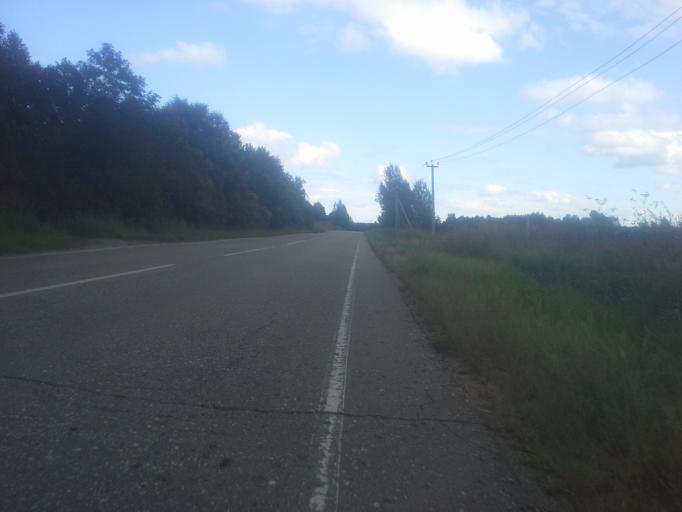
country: RU
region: Moskovskaya
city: Kolyubakino
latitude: 55.6499
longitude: 36.5857
